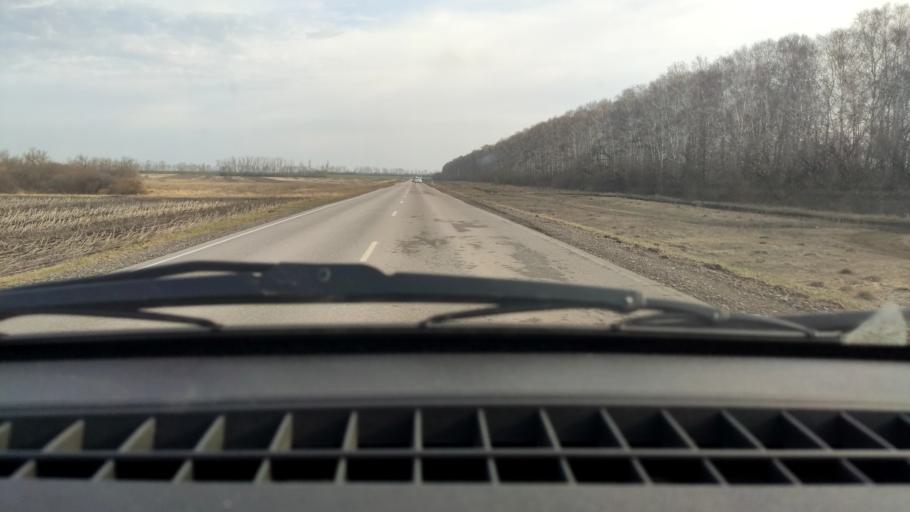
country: RU
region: Bashkortostan
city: Chishmy
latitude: 54.4849
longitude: 55.2714
